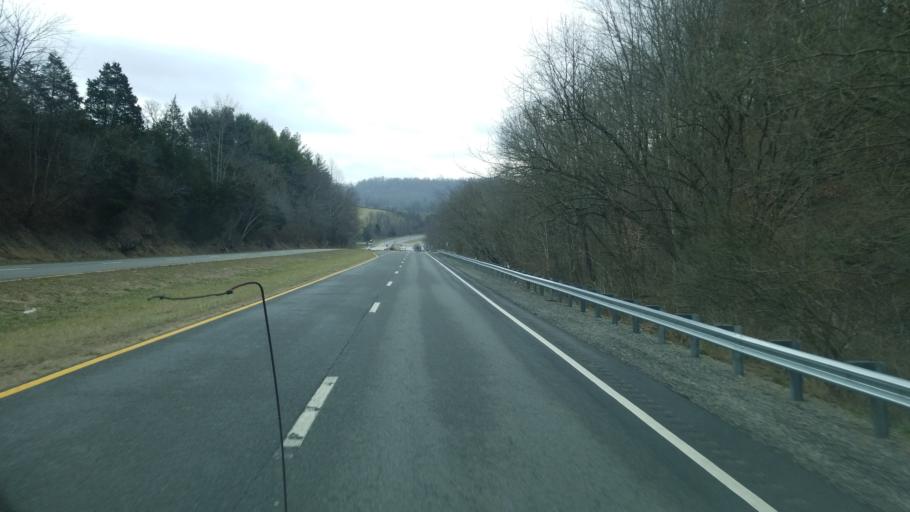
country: US
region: Virginia
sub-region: Giles County
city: Pearisburg
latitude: 37.2691
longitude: -80.7159
